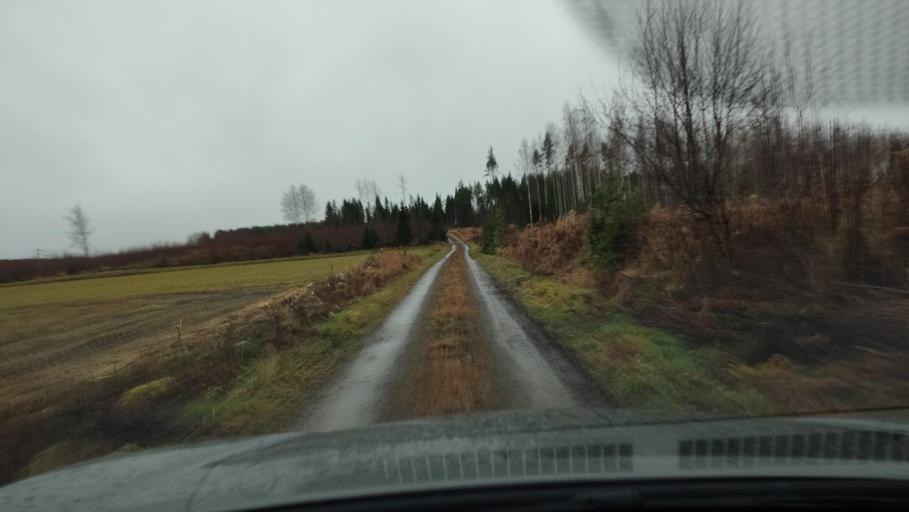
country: FI
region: Southern Ostrobothnia
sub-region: Suupohja
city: Karijoki
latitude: 62.2270
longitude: 21.5516
